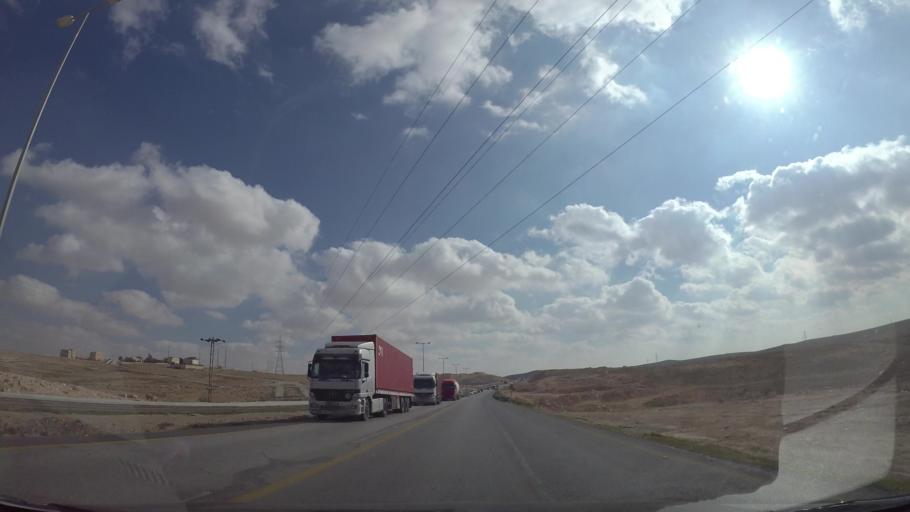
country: JO
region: Amman
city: Al Jizah
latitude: 31.6043
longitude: 35.9989
